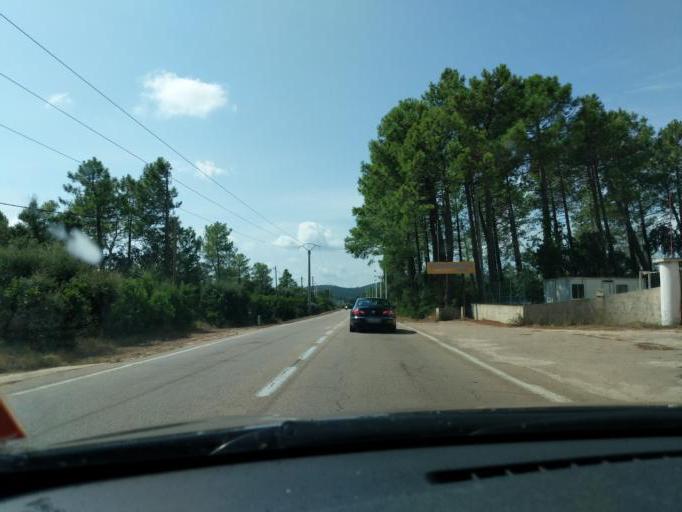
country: FR
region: Corsica
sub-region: Departement de la Corse-du-Sud
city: Porto-Vecchio
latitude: 41.6529
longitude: 9.3006
